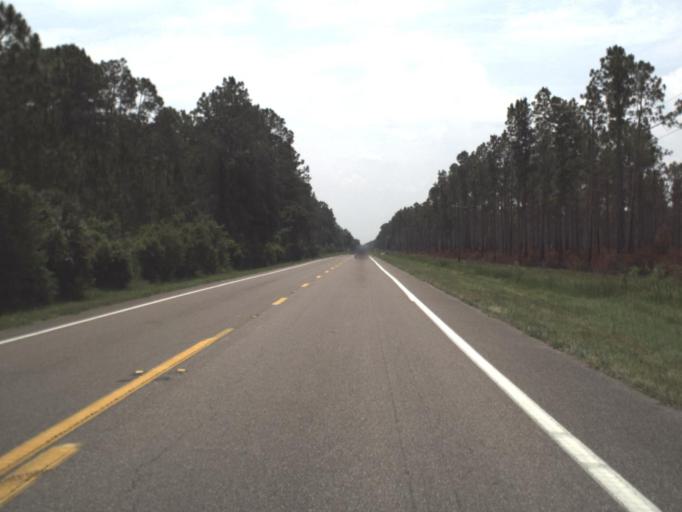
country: US
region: Florida
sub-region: Putnam County
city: Palatka
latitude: 29.5138
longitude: -81.7504
